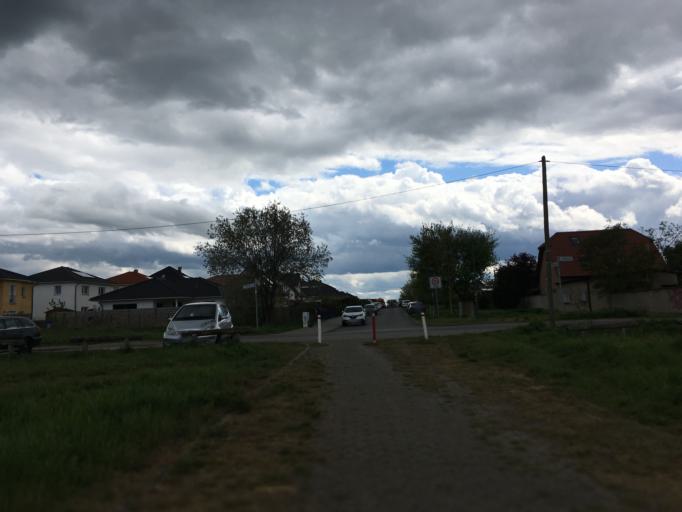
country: DE
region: Berlin
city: Buchholz
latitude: 52.6193
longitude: 13.4181
